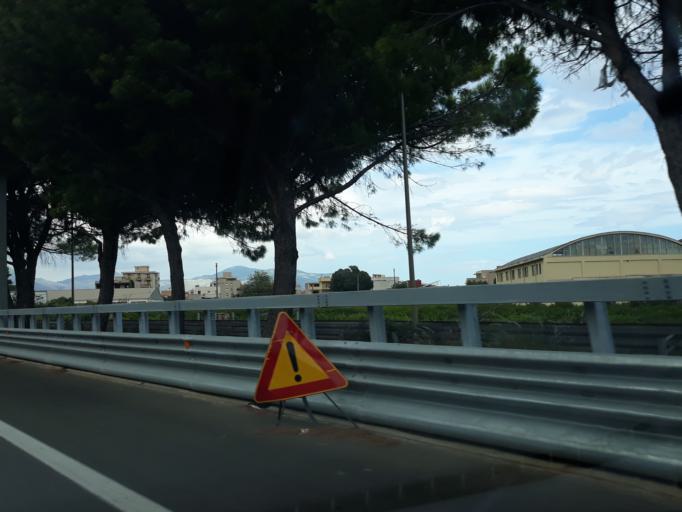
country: IT
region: Sicily
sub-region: Palermo
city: Ciaculli
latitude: 38.0872
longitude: 13.4007
